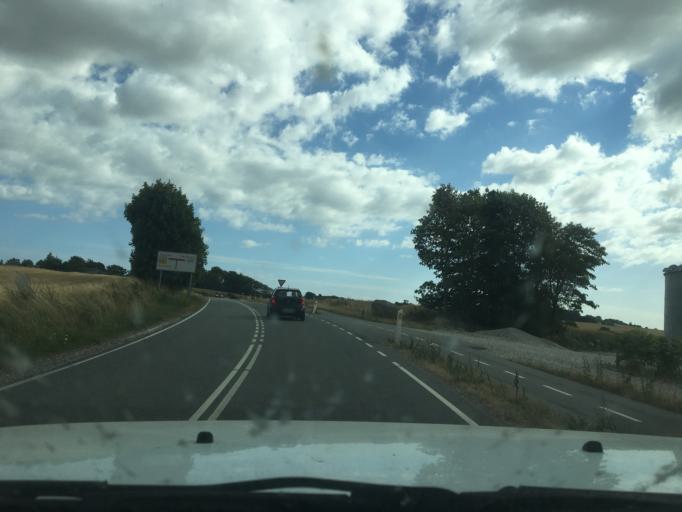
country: DK
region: Central Jutland
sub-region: Arhus Kommune
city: Logten
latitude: 56.2901
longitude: 10.3127
